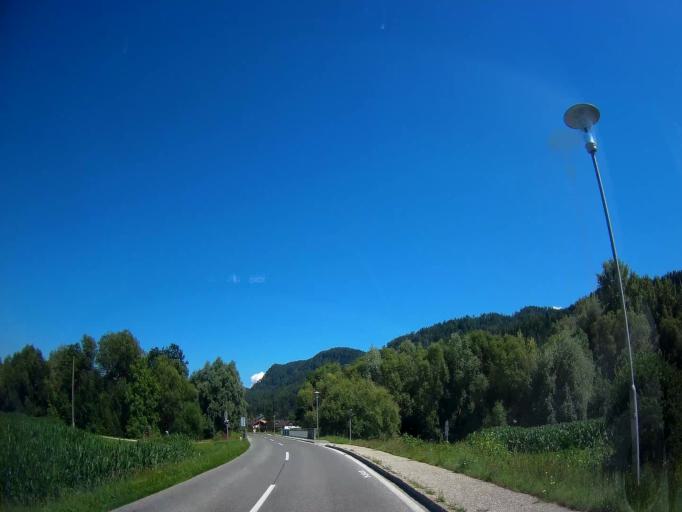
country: AT
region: Carinthia
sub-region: Politischer Bezirk Klagenfurt Land
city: Ebenthal
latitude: 46.6062
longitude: 14.4003
